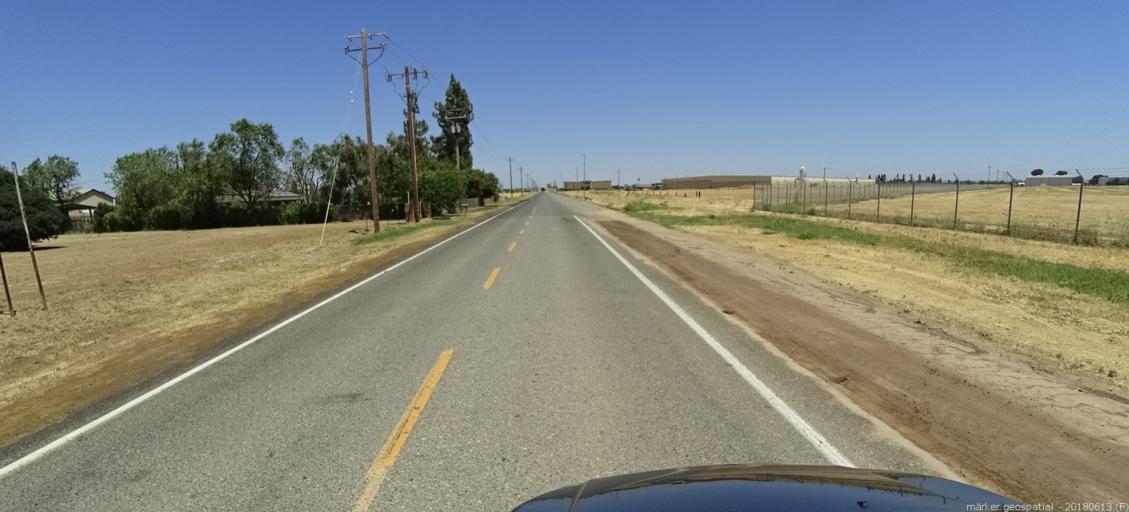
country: US
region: California
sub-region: Madera County
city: Madera Acres
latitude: 36.9965
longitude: -120.1167
